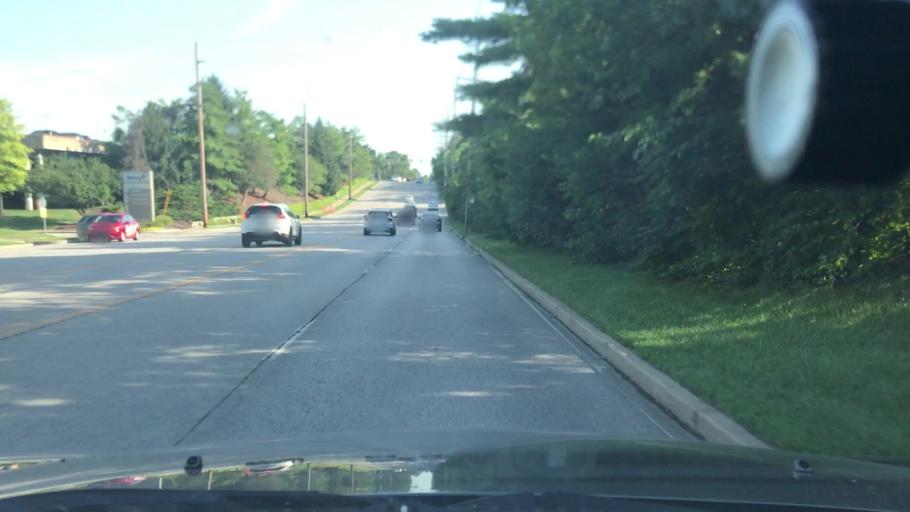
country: US
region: Missouri
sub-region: Saint Louis County
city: Creve Coeur
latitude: 38.6442
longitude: -90.4433
